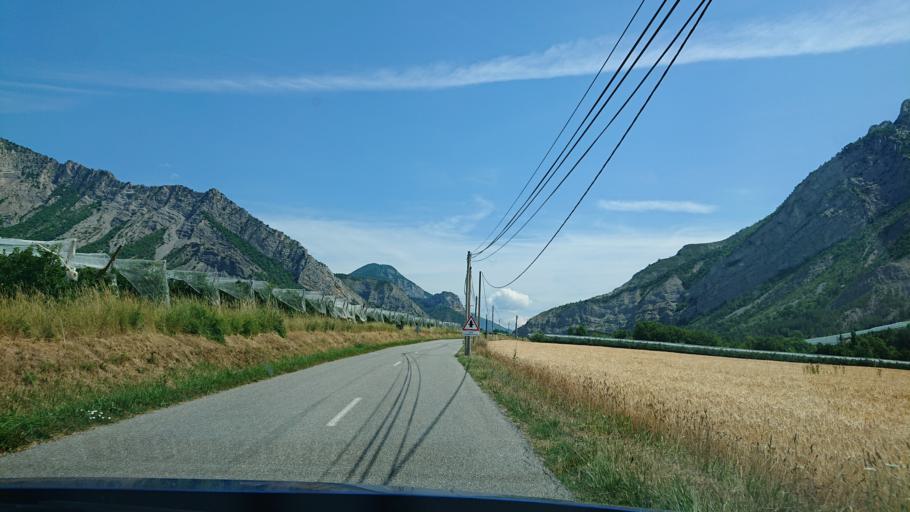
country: FR
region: Provence-Alpes-Cote d'Azur
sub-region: Departement des Hautes-Alpes
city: Tallard
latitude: 44.3528
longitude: 6.0410
